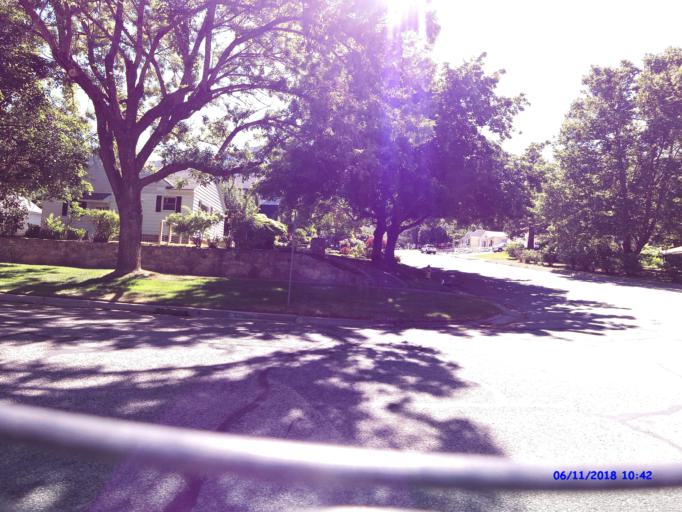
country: US
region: Utah
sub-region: Weber County
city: Ogden
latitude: 41.2224
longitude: -111.9372
